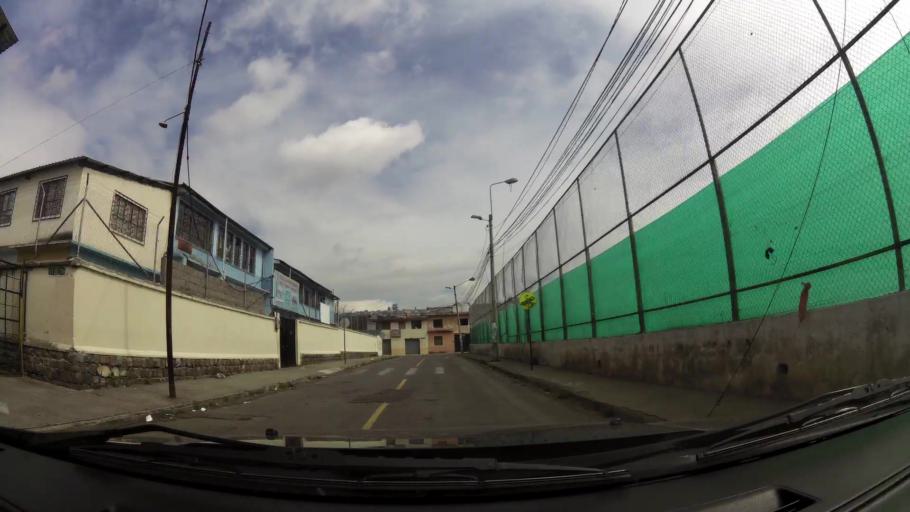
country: EC
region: Pichincha
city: Quito
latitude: -0.2175
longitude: -78.4895
